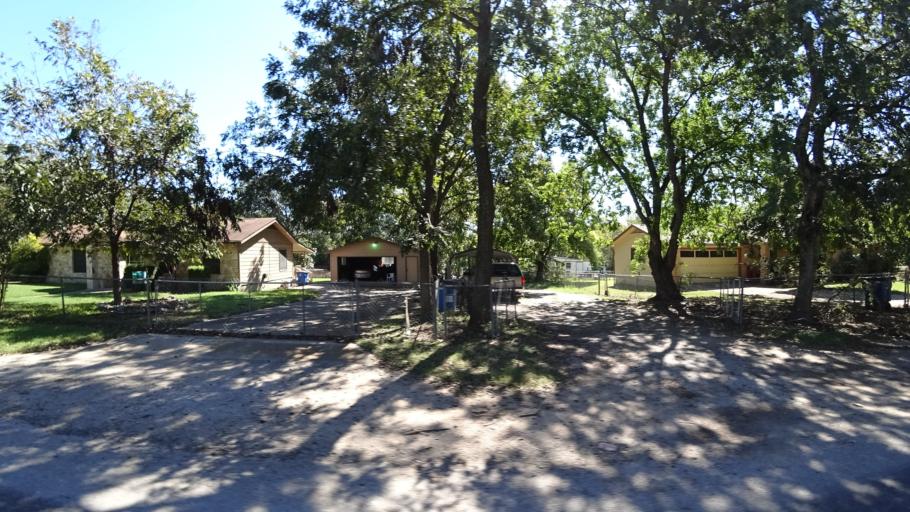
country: US
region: Texas
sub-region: Travis County
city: Austin
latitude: 30.1861
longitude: -97.6897
